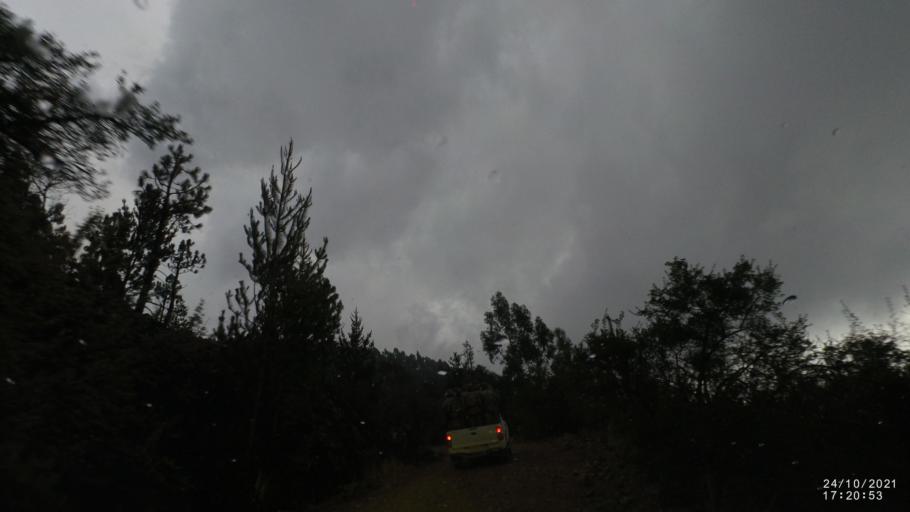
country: BO
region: Cochabamba
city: Cochabamba
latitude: -17.3273
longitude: -66.1362
